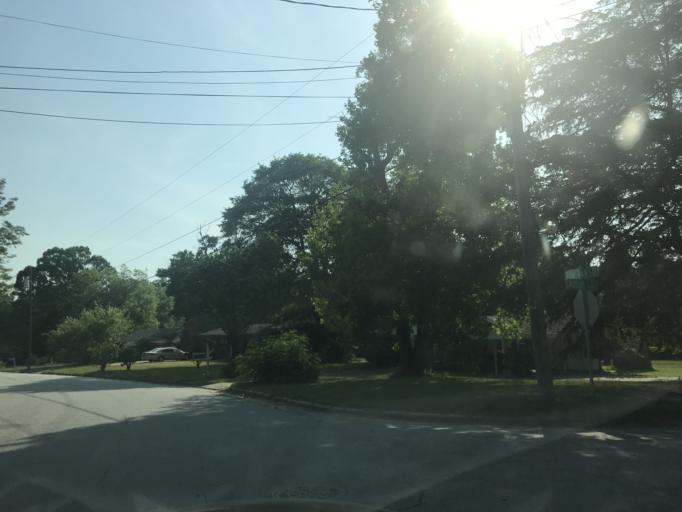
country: US
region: North Carolina
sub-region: Wake County
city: Raleigh
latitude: 35.7694
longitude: -78.5953
